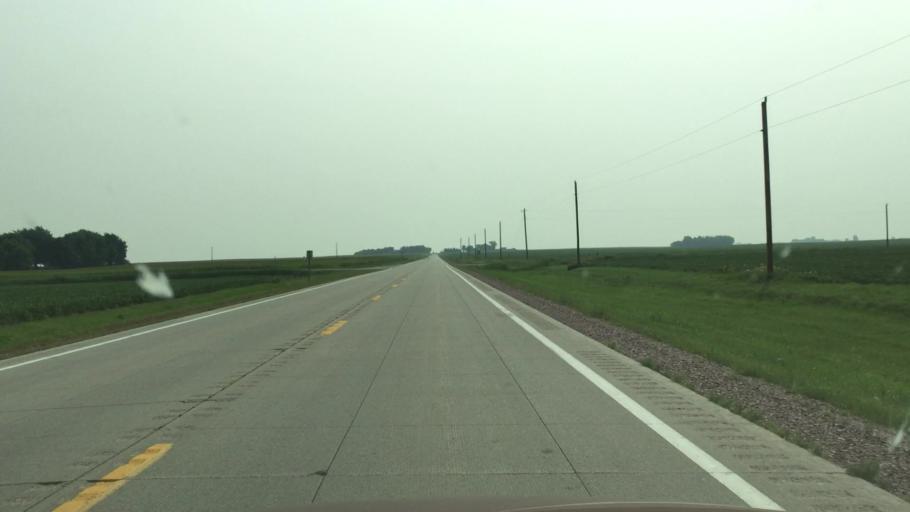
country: US
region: Iowa
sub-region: Osceola County
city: Sibley
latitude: 43.4327
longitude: -95.6848
